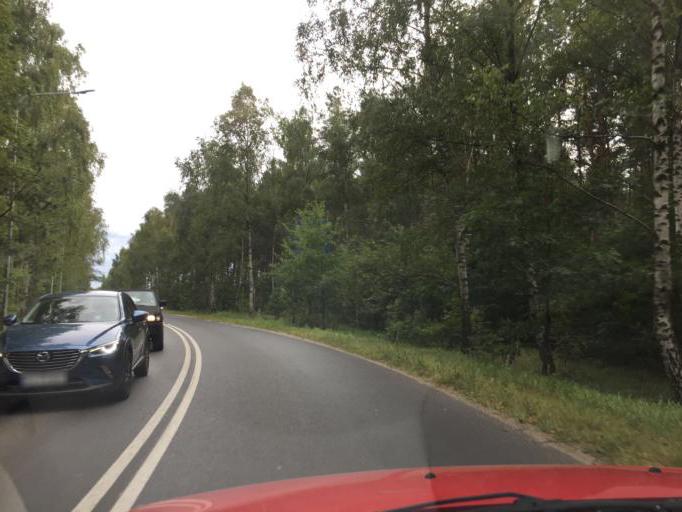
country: PL
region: Greater Poland Voivodeship
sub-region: Powiat poznanski
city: Baranowo
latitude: 52.4125
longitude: 16.7905
